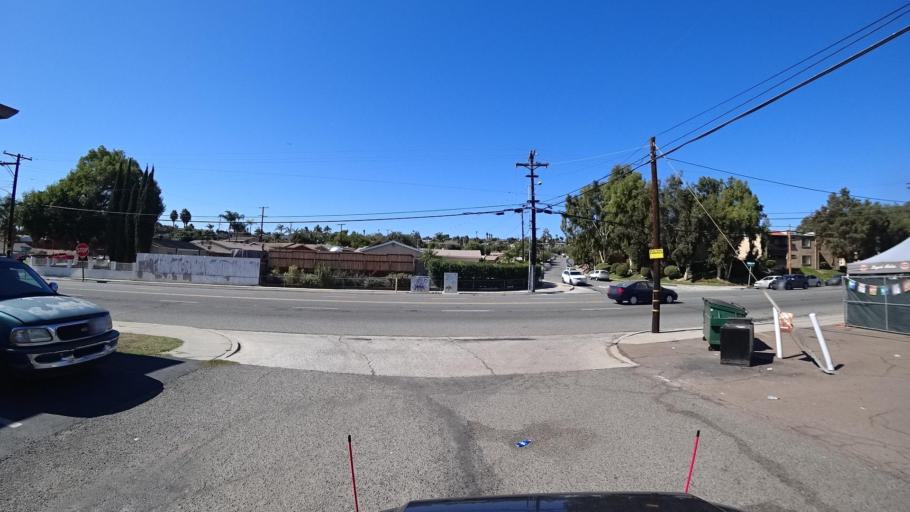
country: US
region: California
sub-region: San Diego County
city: La Presa
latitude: 32.7128
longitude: -117.0165
